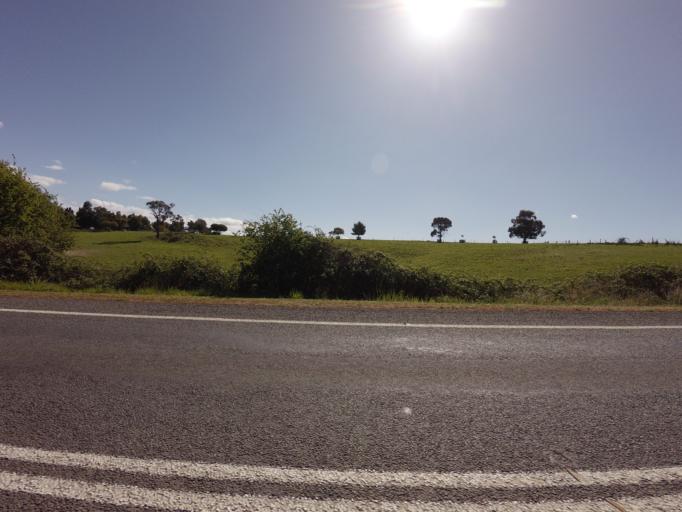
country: AU
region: Tasmania
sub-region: Derwent Valley
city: New Norfolk
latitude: -42.7003
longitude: 146.9424
